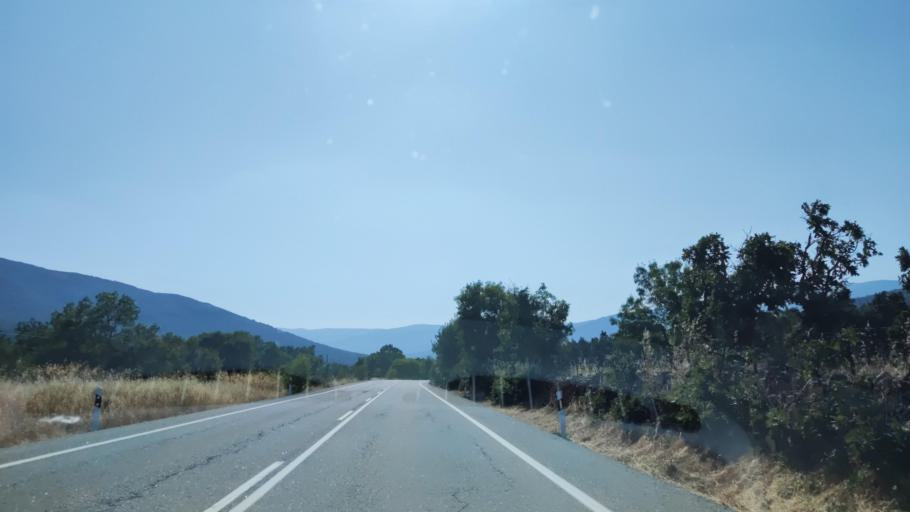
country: ES
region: Madrid
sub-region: Provincia de Madrid
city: Canencia
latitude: 40.9468
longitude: -3.7406
